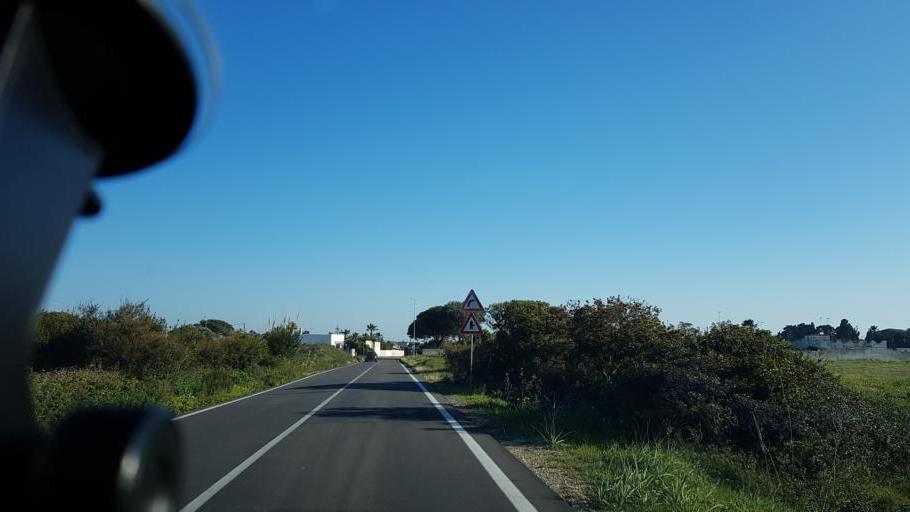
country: IT
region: Apulia
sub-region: Provincia di Lecce
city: Merine
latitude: 40.4328
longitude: 18.2412
